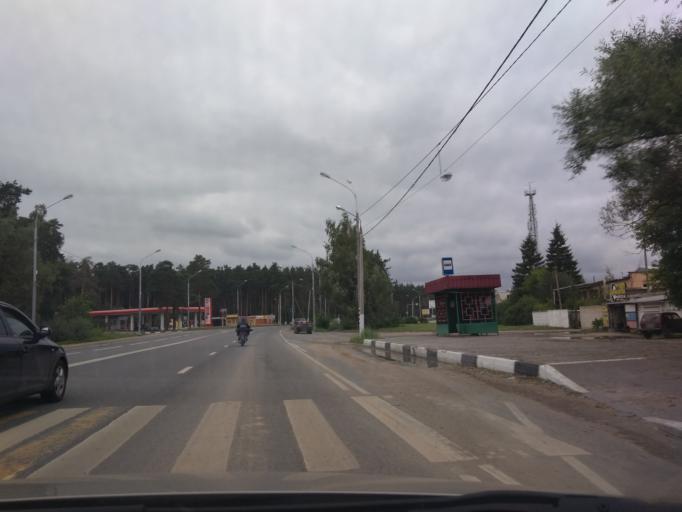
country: RU
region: Moskovskaya
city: Orekhovo-Zuyevo
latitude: 55.8276
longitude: 38.9636
